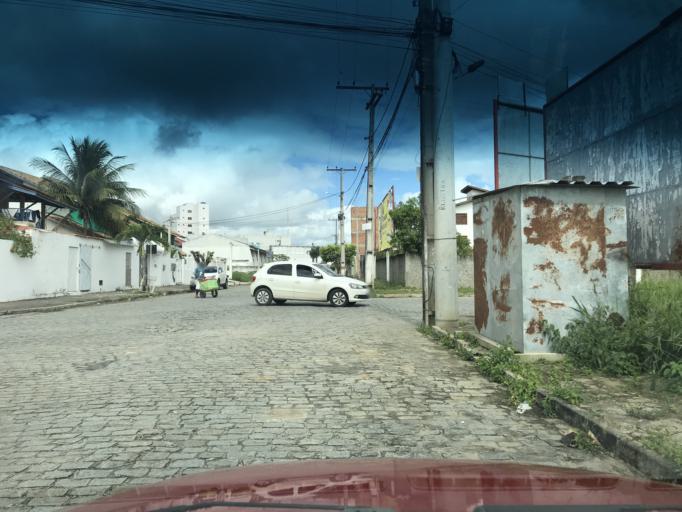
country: BR
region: Bahia
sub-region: Santo Antonio De Jesus
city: Santo Antonio de Jesus
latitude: -12.9634
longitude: -39.2634
